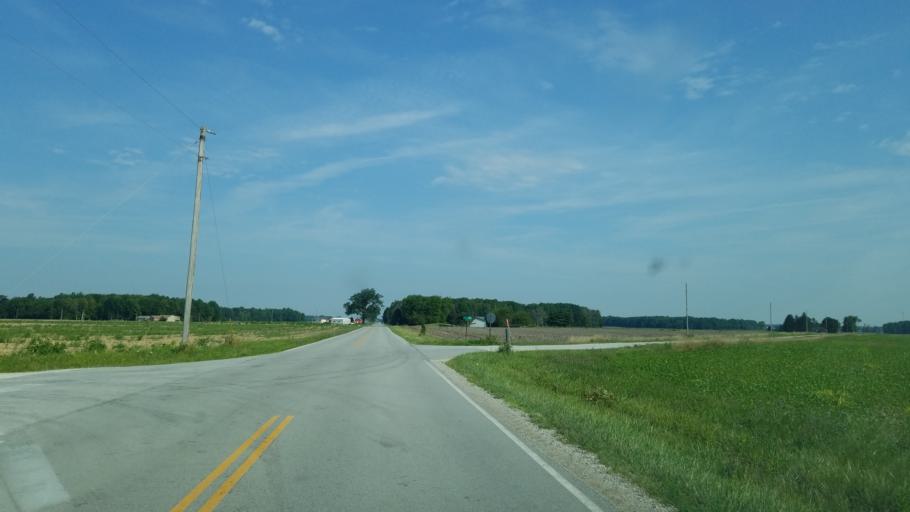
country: US
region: Ohio
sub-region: Huron County
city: Willard
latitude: 41.0193
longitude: -82.8619
